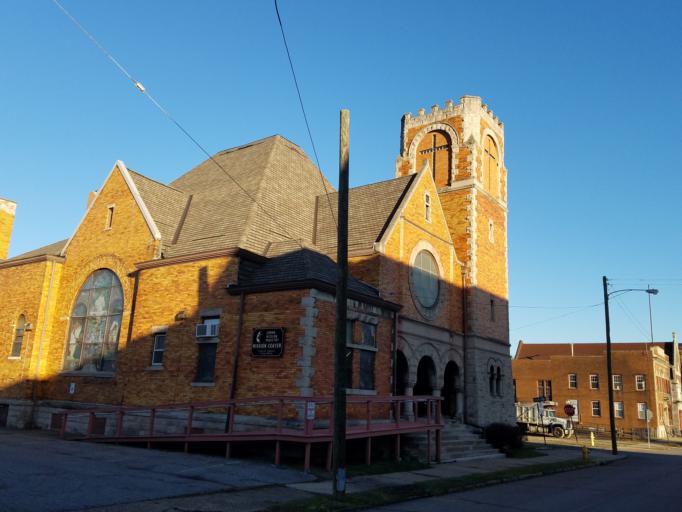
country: US
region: Ohio
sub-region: Jefferson County
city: Steubenville
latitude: 40.3643
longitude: -80.6158
